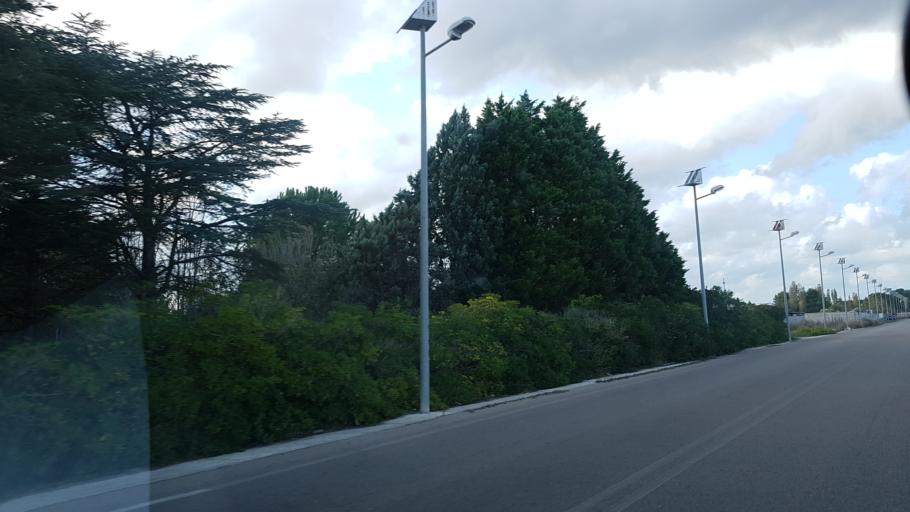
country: IT
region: Apulia
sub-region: Provincia di Brindisi
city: San Pietro Vernotico
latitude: 40.4949
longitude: 18.0079
